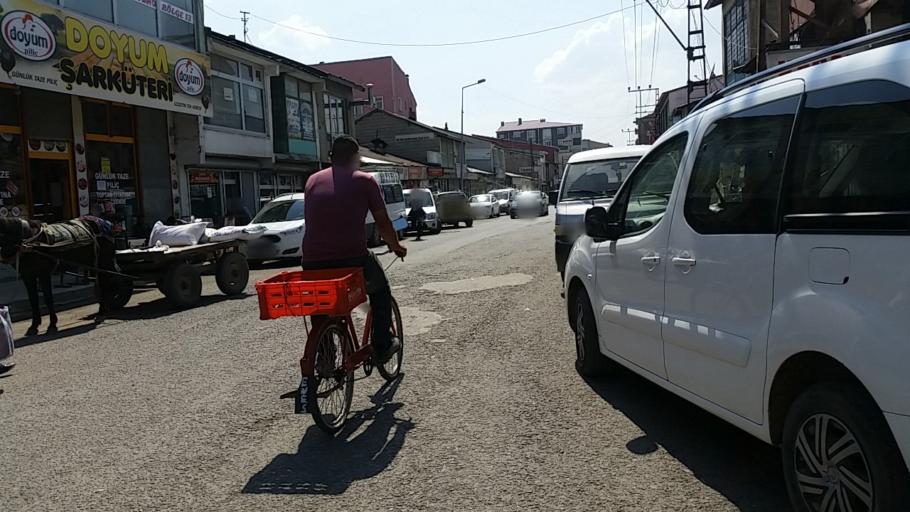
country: TR
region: Agri
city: Agri
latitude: 39.7144
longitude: 43.0530
